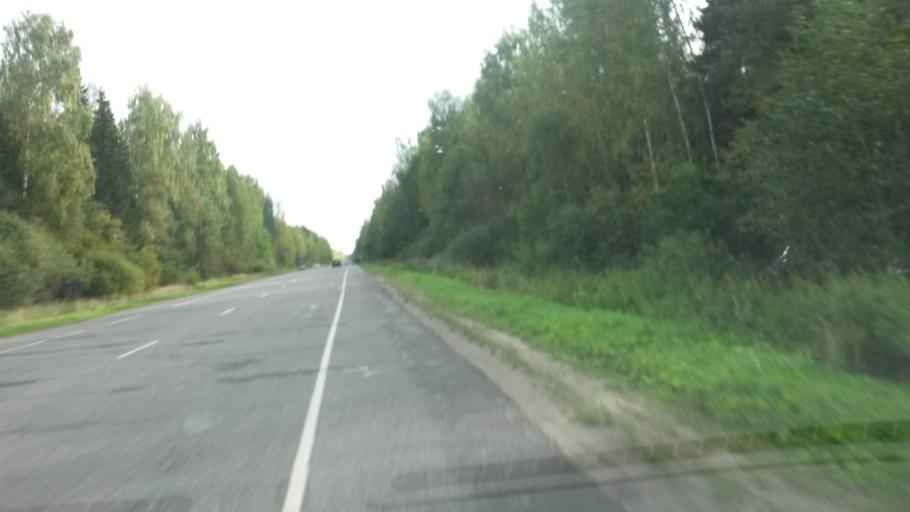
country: RU
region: Ivanovo
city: Kaminskiy
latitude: 57.0798
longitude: 41.5081
